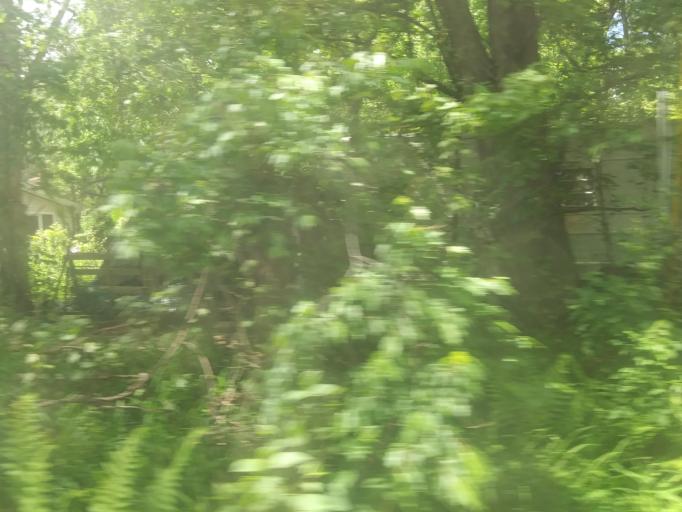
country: US
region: Massachusetts
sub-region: Franklin County
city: Shelburne Falls
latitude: 42.5787
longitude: -72.7555
